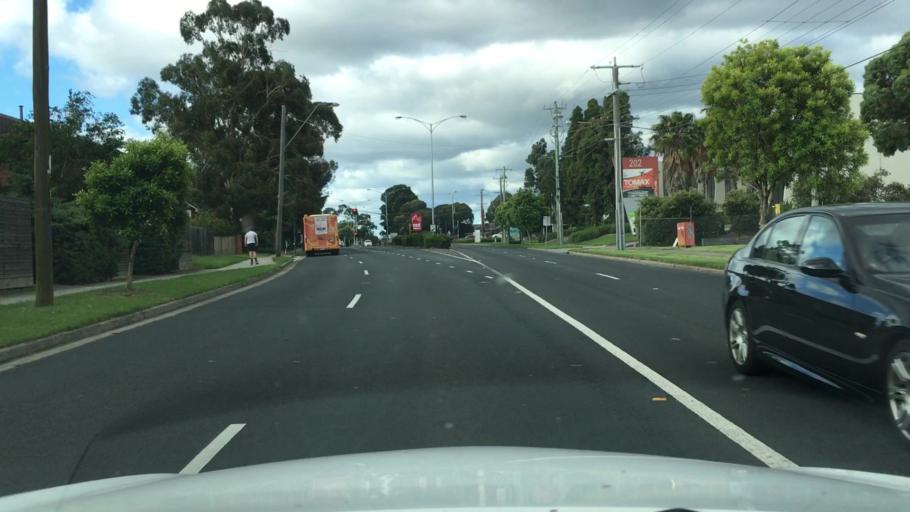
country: AU
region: Victoria
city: Clayton
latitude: -37.9008
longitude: 145.1243
